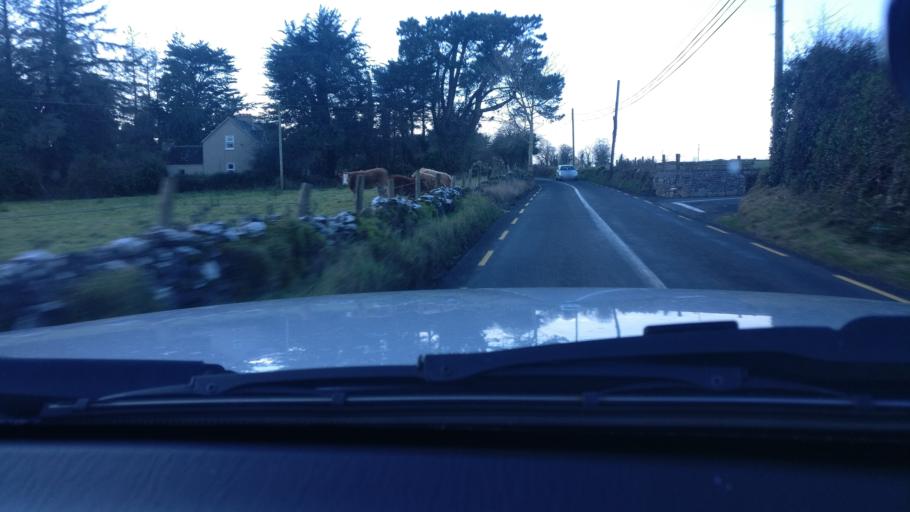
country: IE
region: Connaught
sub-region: County Galway
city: Loughrea
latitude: 53.2274
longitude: -8.4152
